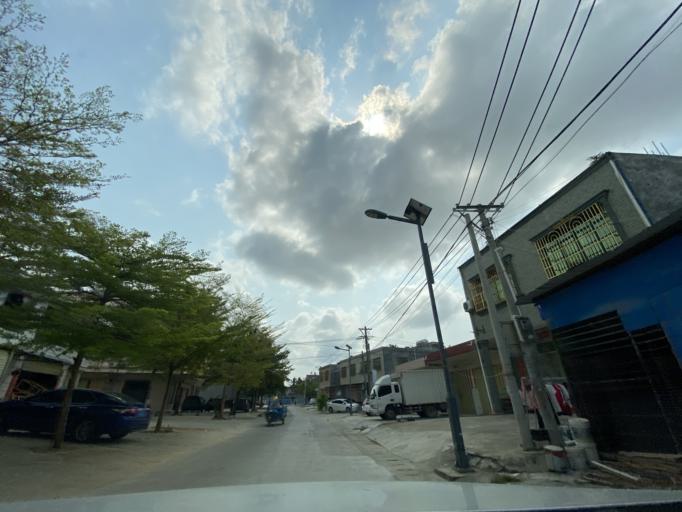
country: CN
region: Hainan
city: Yingzhou
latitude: 18.4214
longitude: 109.8525
